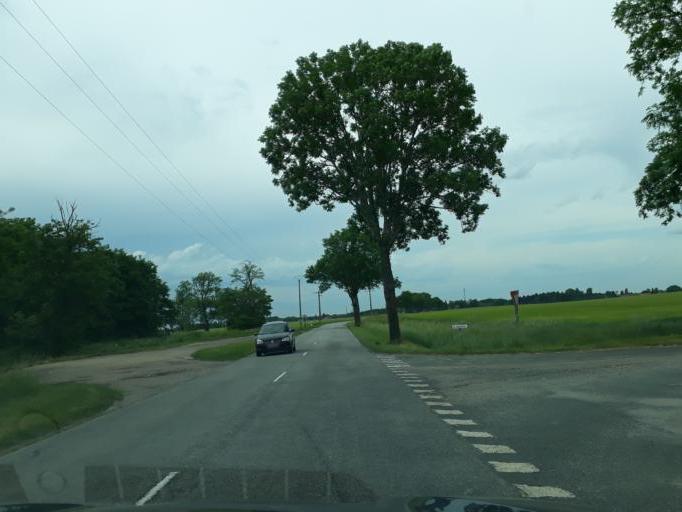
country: FR
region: Centre
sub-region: Departement du Loiret
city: Vienne-en-Val
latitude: 47.8257
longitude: 2.1497
